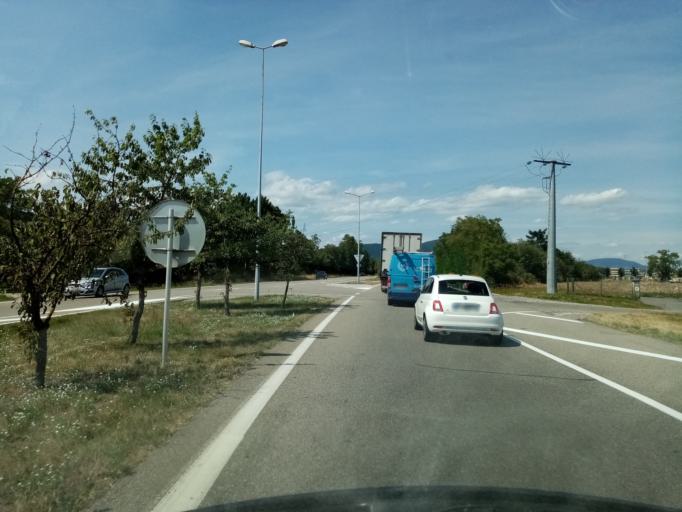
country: FR
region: Alsace
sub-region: Departement du Bas-Rhin
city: Selestat
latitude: 48.2570
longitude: 7.4239
